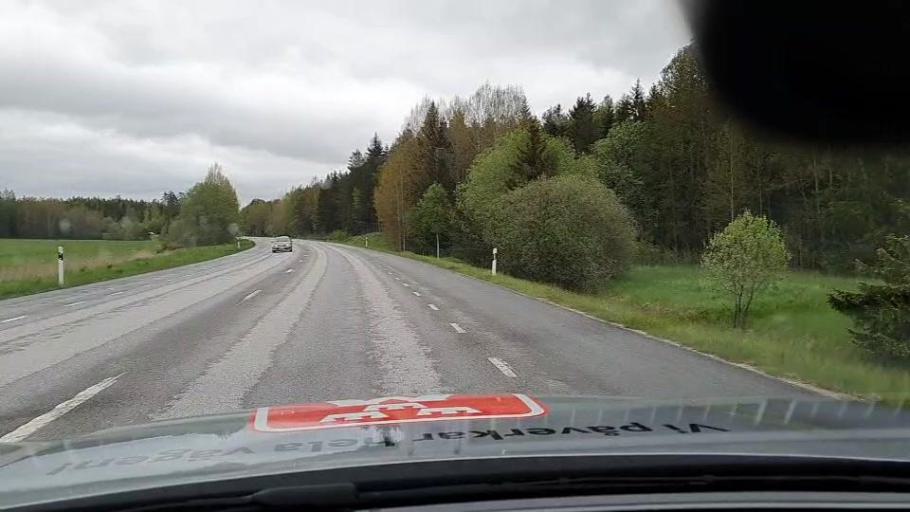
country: SE
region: Soedermanland
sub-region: Nykopings Kommun
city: Svalsta
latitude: 58.7430
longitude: 16.9227
